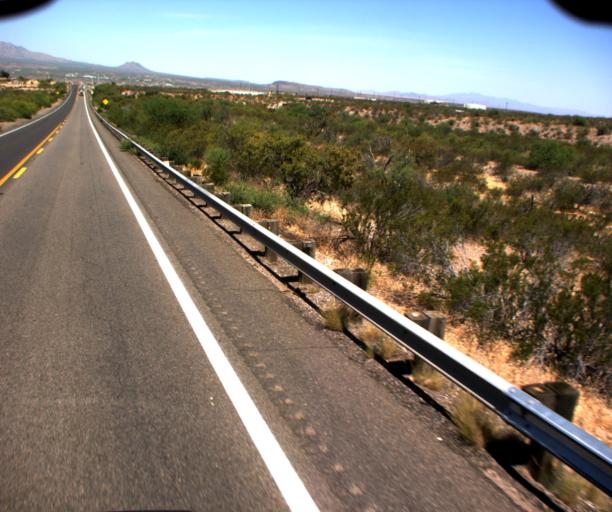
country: US
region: Arizona
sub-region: Gila County
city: Peridot
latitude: 33.2910
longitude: -110.4197
